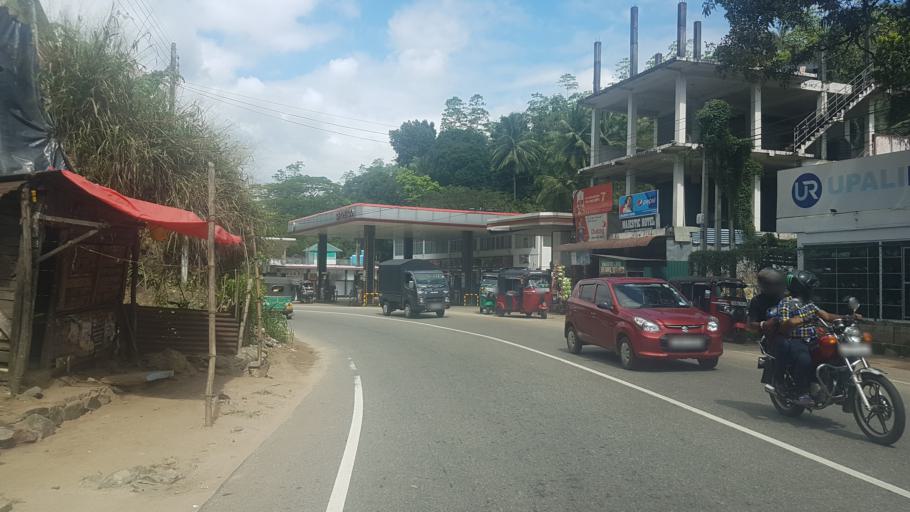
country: LK
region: Central
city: Gampola
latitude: 7.2087
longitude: 80.5989
